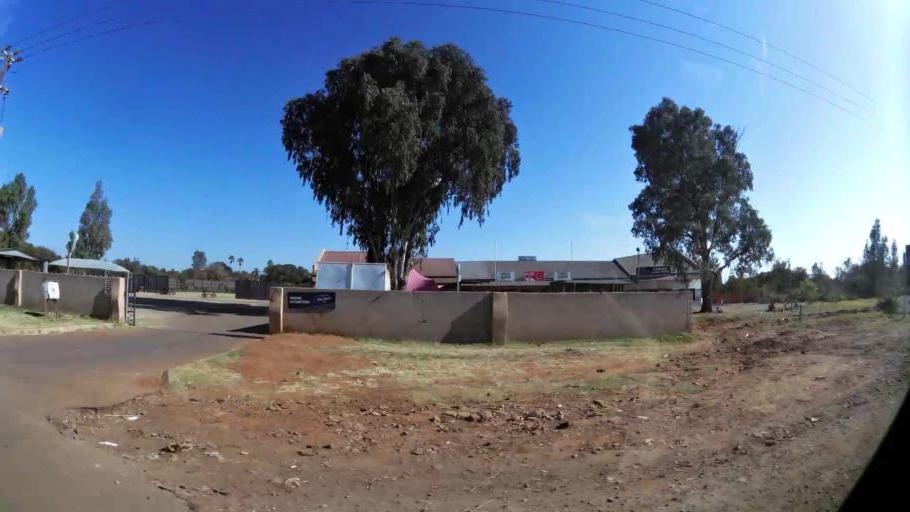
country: ZA
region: North-West
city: Ga-Rankuwa
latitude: -25.6591
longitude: 28.0823
